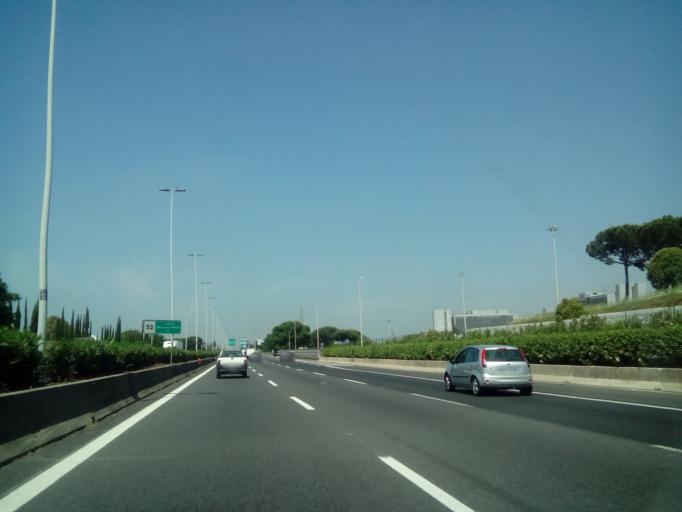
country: IT
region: Latium
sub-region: Citta metropolitana di Roma Capitale
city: Selcetta
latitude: 41.7968
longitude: 12.4879
